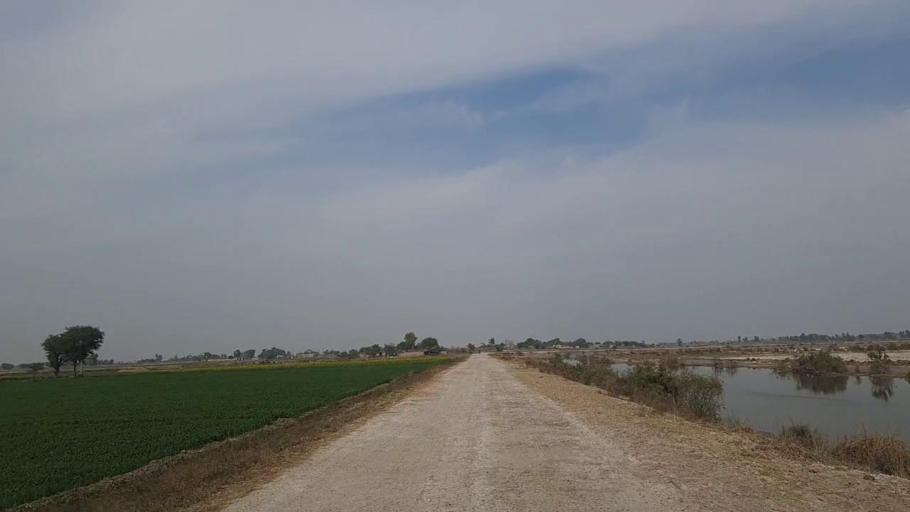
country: PK
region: Sindh
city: Daur
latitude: 26.4750
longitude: 68.4024
